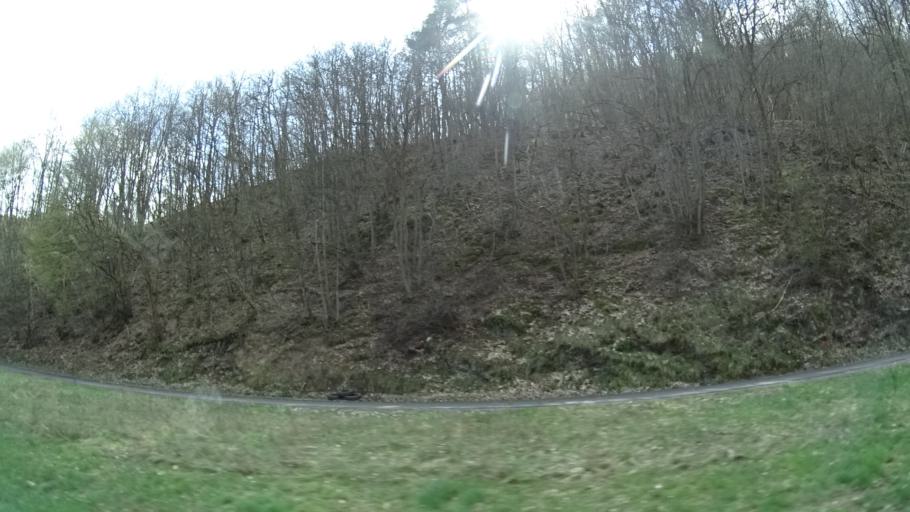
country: DE
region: Rheinland-Pfalz
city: Hintertiefenbach
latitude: 49.7472
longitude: 7.3735
